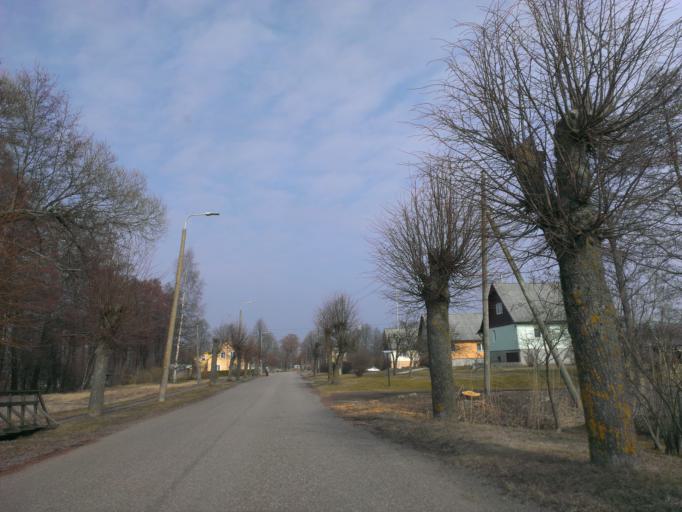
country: LV
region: Salacgrivas
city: Ainazi
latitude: 57.8720
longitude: 24.3607
